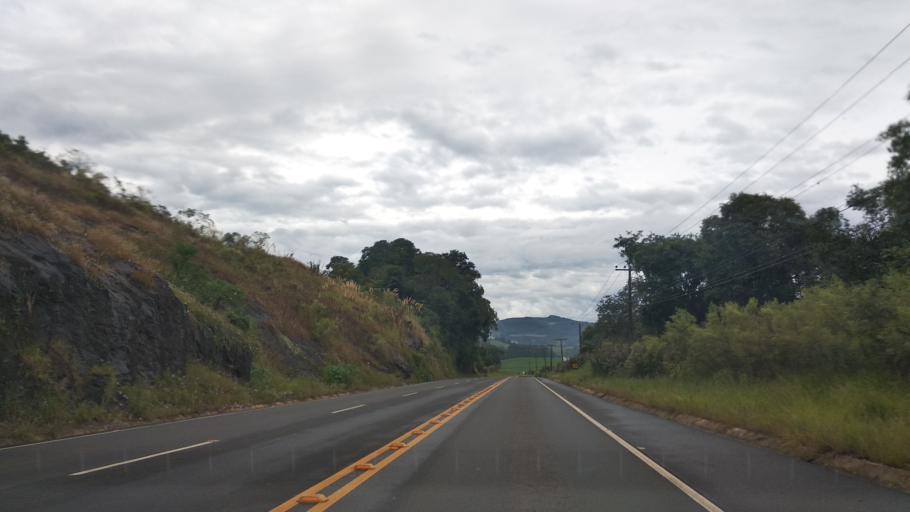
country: BR
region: Santa Catarina
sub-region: Videira
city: Videira
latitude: -27.0629
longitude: -51.2338
